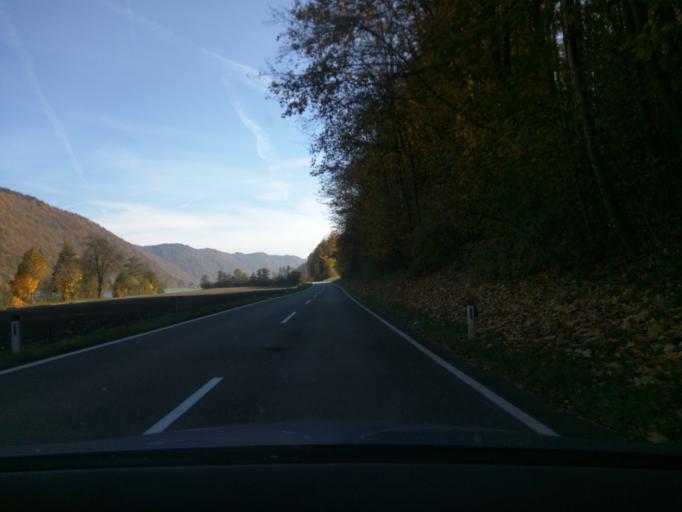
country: DE
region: Bavaria
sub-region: Lower Bavaria
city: Untergriesbach
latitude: 48.5265
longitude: 13.6829
